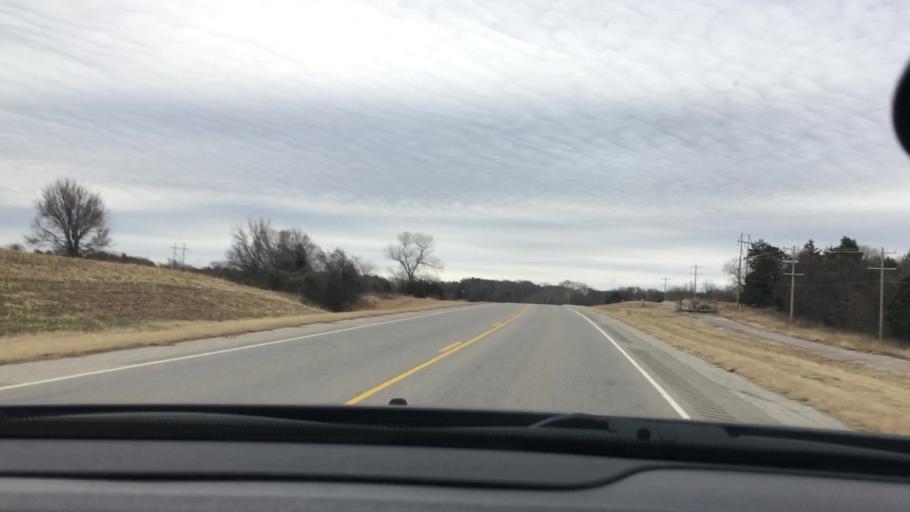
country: US
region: Oklahoma
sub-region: Johnston County
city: Tishomingo
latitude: 34.2336
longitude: -96.7870
